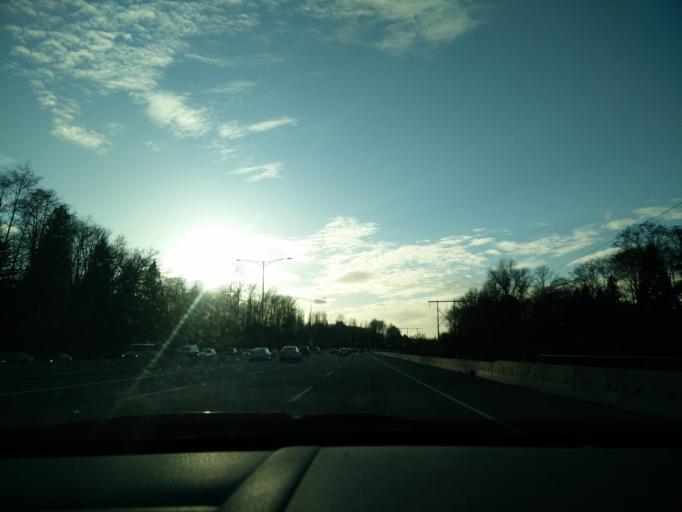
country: CA
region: British Columbia
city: Burnaby
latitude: 49.2371
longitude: -122.9402
